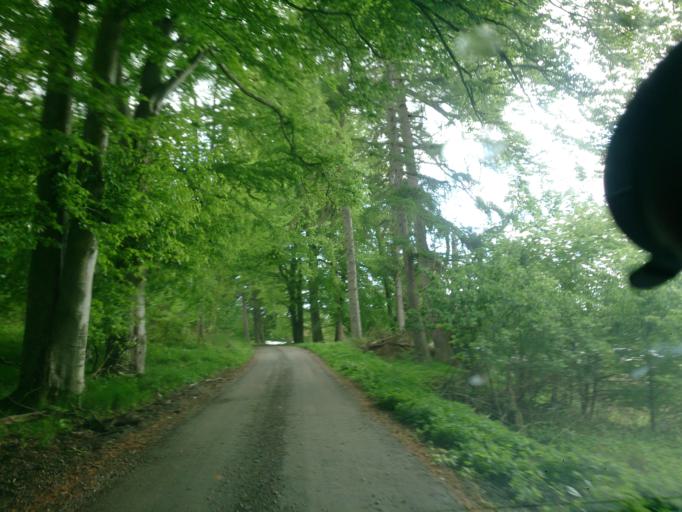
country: SE
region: Skane
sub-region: Sjobo Kommun
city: Sjoebo
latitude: 55.5610
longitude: 13.7072
